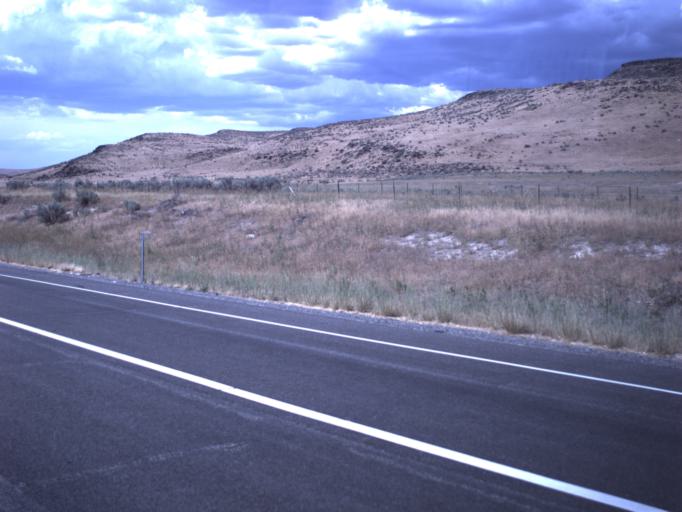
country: US
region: Idaho
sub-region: Oneida County
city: Malad City
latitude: 41.8986
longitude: -112.5779
